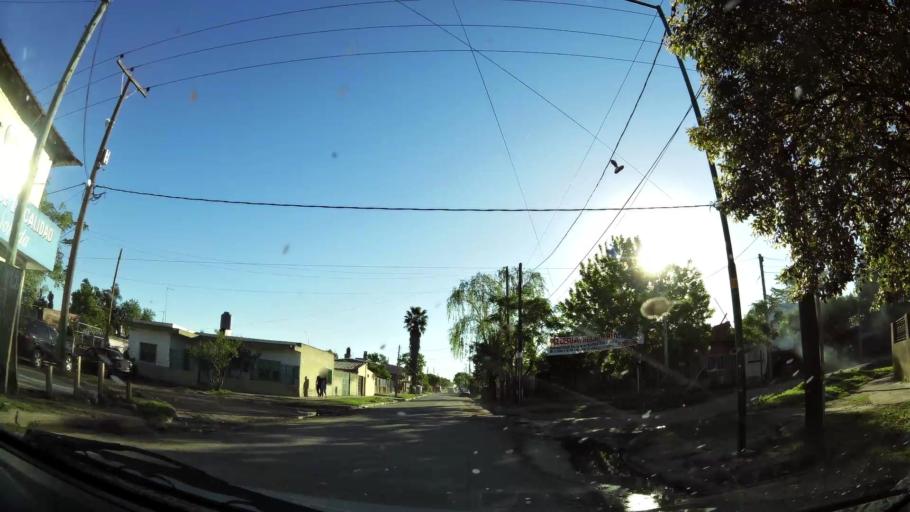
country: AR
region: Buenos Aires
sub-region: Partido de Almirante Brown
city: Adrogue
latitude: -34.7666
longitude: -58.3335
